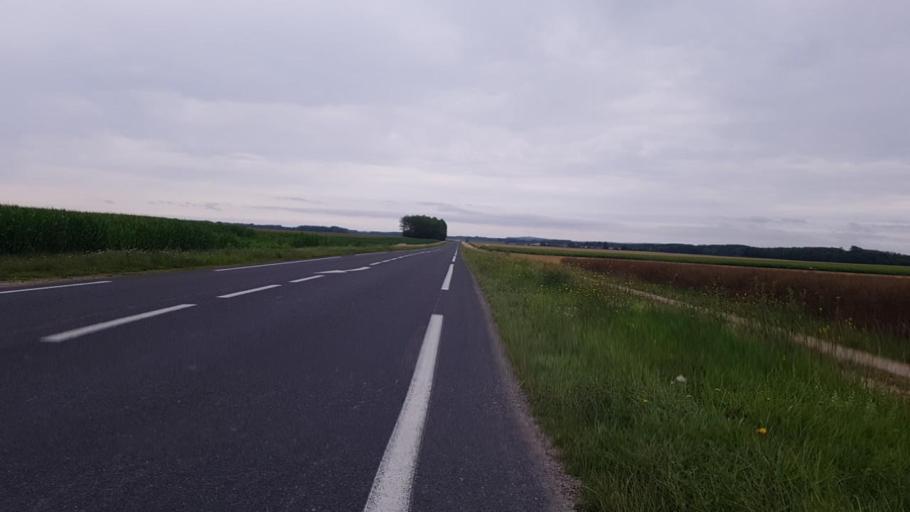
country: FR
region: Champagne-Ardenne
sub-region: Departement de la Marne
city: Pargny-sur-Saulx
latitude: 48.7604
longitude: 4.7767
